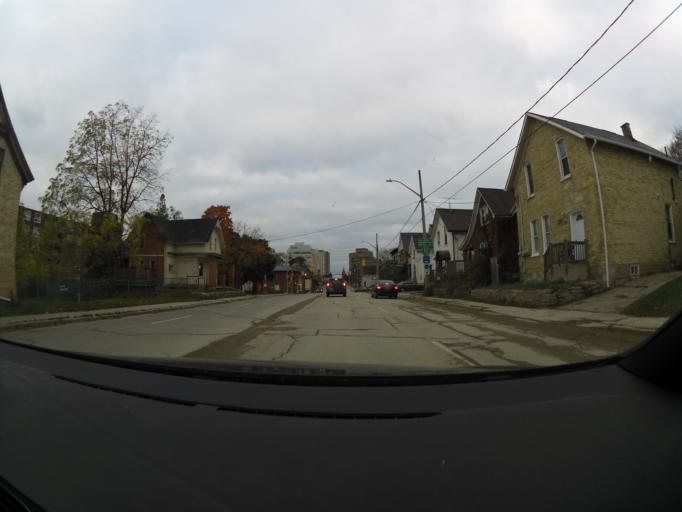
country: CA
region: Ontario
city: Kitchener
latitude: 43.4489
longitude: -80.4807
